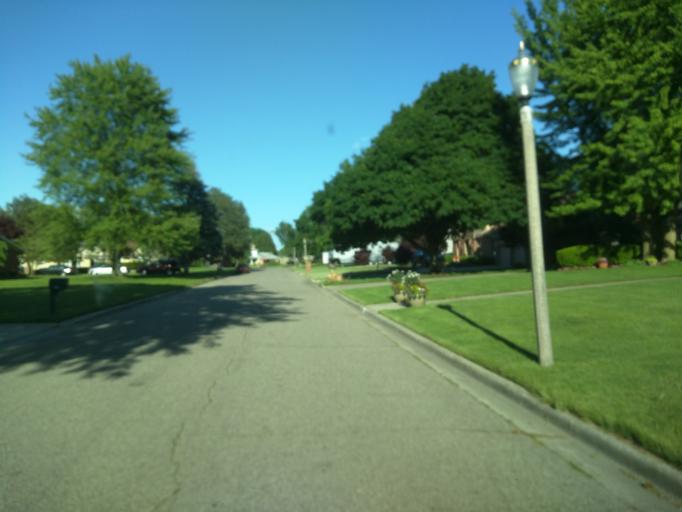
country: US
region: Michigan
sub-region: Eaton County
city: Waverly
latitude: 42.7516
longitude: -84.6110
